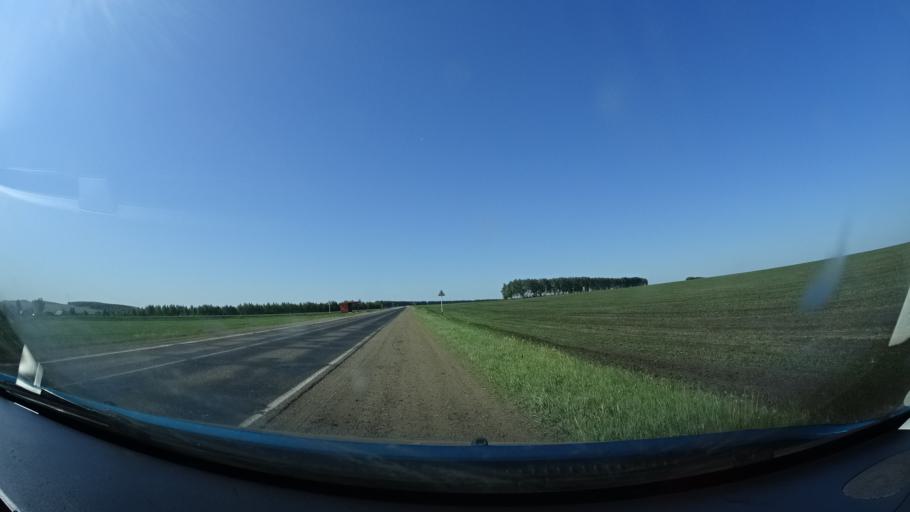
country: RU
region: Bashkortostan
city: Starobaltachevo
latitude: 55.9211
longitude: 55.7829
